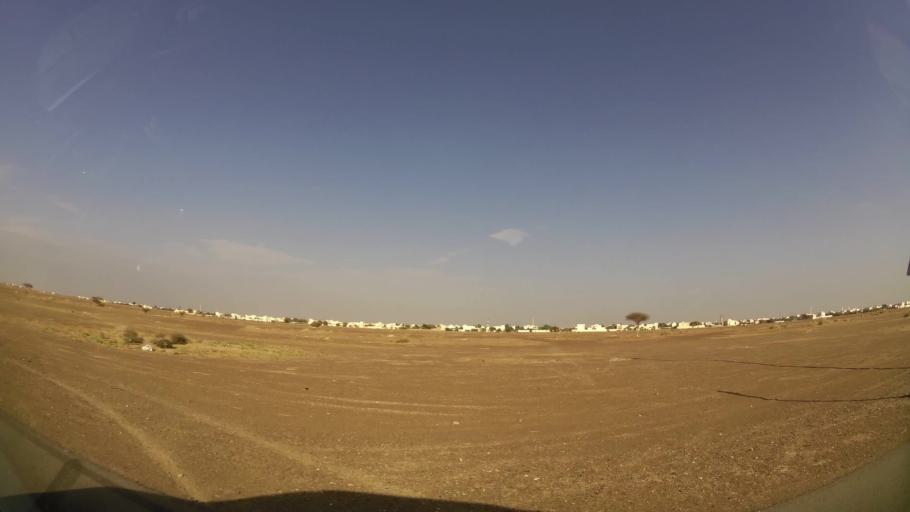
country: AE
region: Abu Dhabi
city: Al Ain
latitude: 24.0778
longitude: 55.8546
